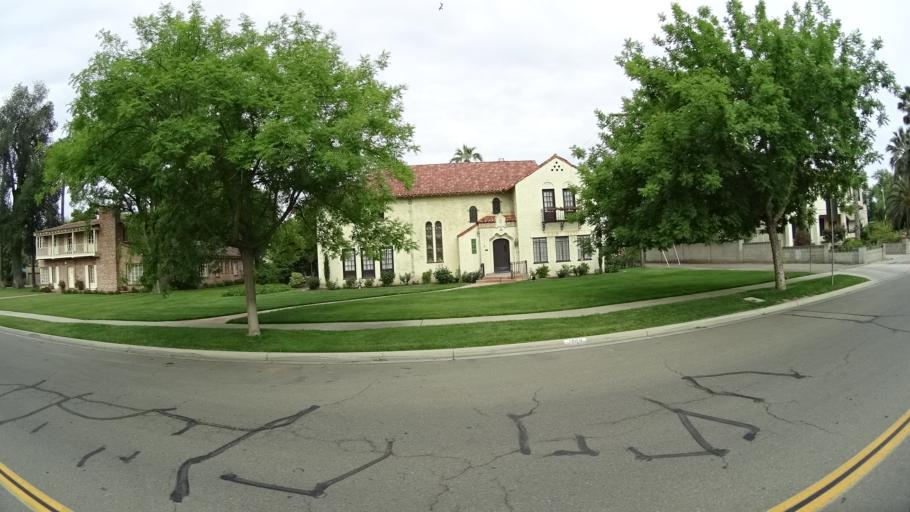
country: US
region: California
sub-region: Kings County
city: Hanford
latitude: 36.3420
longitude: -119.6476
